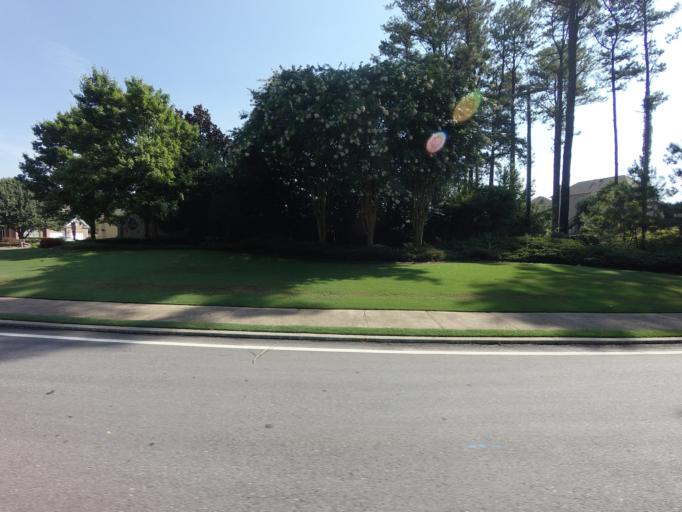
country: US
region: Georgia
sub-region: Fulton County
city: Johns Creek
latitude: 34.0577
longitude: -84.2047
